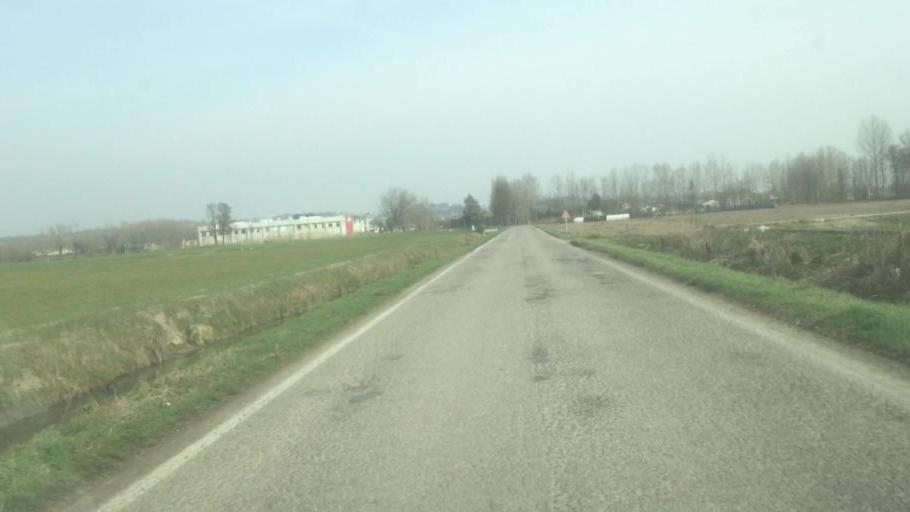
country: IT
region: Lombardy
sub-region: Provincia di Mantova
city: Cerlongo
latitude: 45.2949
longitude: 10.6347
